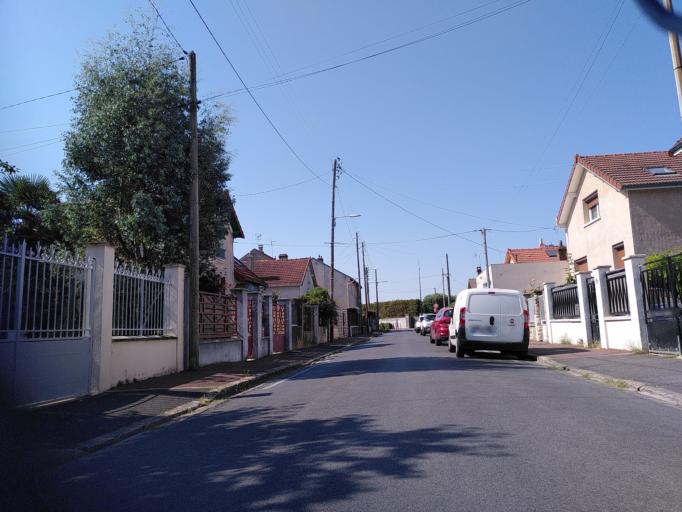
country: FR
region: Ile-de-France
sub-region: Departement de l'Essonne
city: Paray-Vieille-Poste
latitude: 48.6970
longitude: 2.3600
